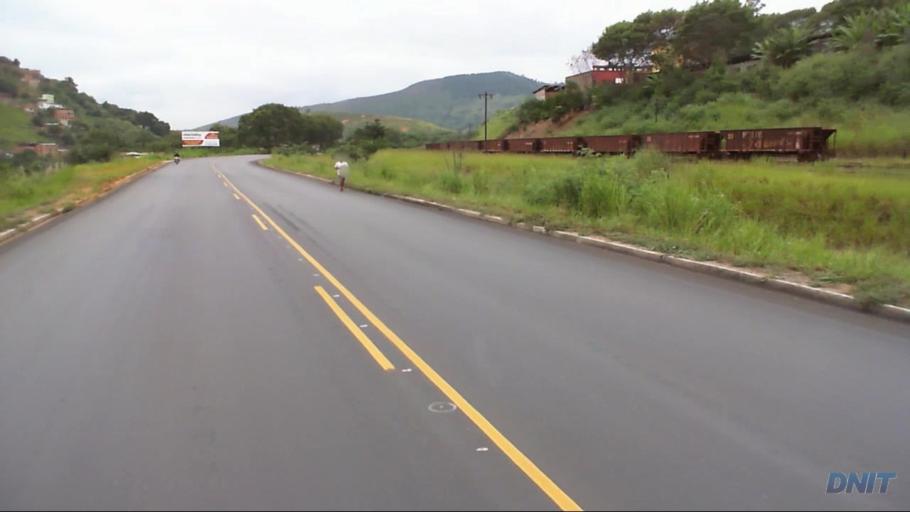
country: BR
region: Minas Gerais
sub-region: Coronel Fabriciano
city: Coronel Fabriciano
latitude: -19.5268
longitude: -42.6358
